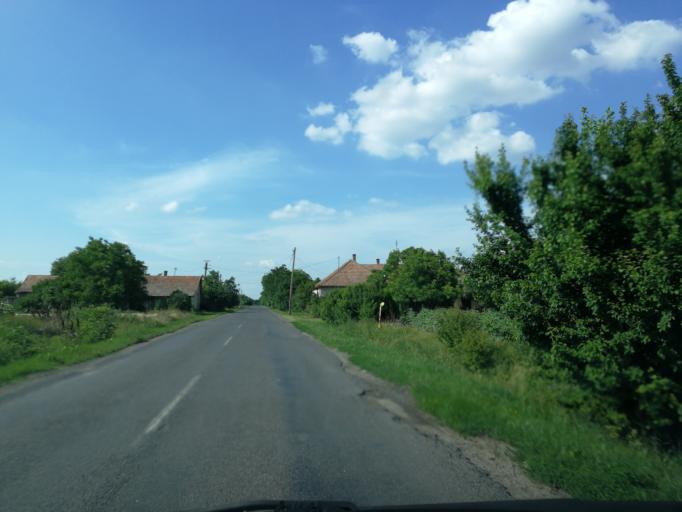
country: HU
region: Bacs-Kiskun
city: Kalocsa
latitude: 46.4985
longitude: 19.0526
